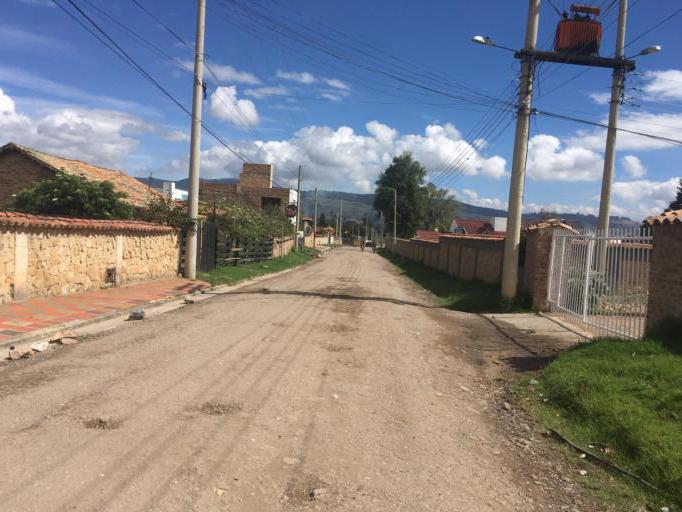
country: CO
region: Boyaca
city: Firavitoba
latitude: 5.6648
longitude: -72.9604
